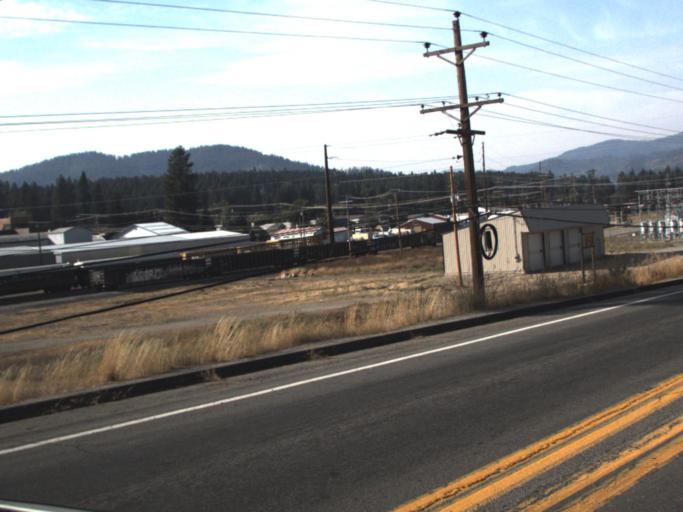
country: US
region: Washington
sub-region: Pend Oreille County
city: Newport
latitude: 48.1801
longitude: -117.0396
